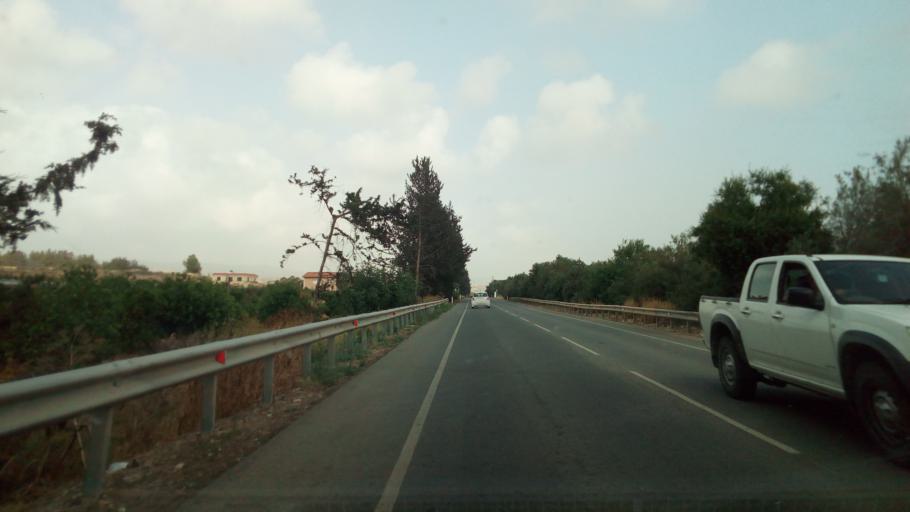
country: CY
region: Pafos
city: Mesogi
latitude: 34.7188
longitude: 32.5396
